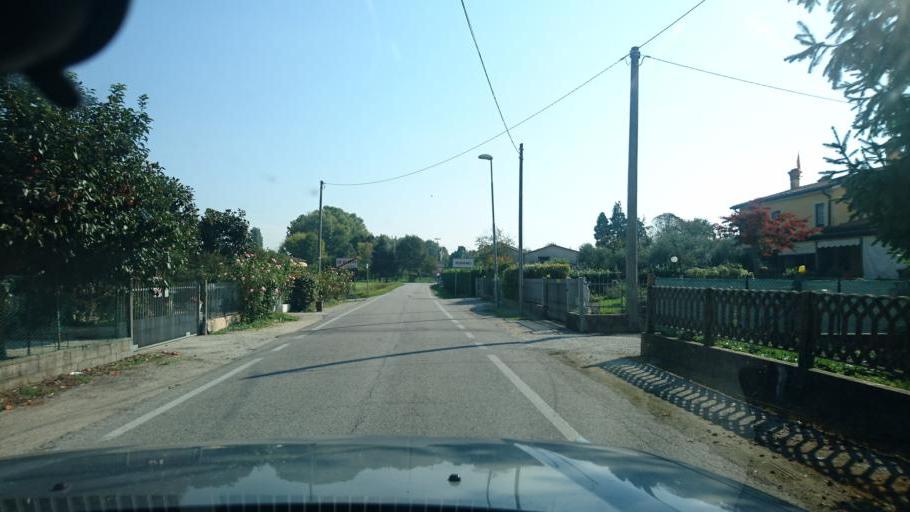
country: IT
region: Veneto
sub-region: Provincia di Padova
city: Rubano
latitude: 45.4248
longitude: 11.7760
